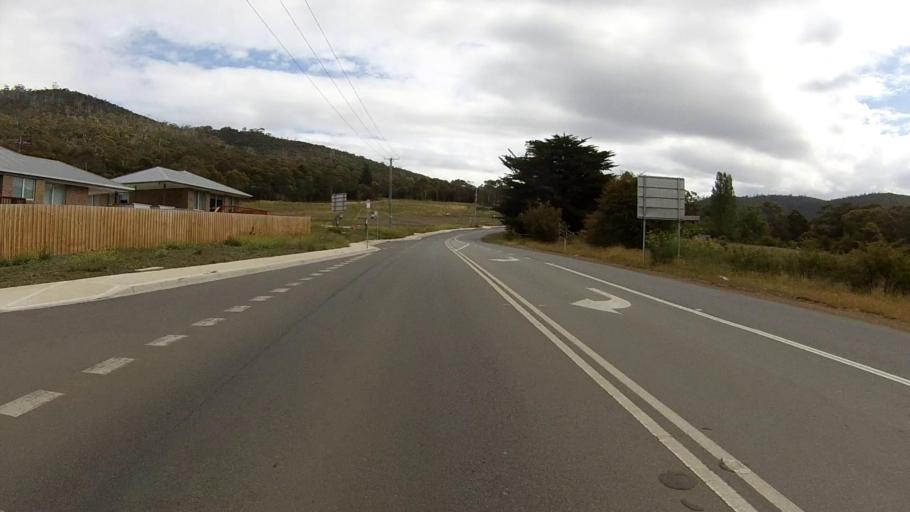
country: AU
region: Tasmania
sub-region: Clarence
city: Cambridge
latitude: -42.8381
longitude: 147.4384
